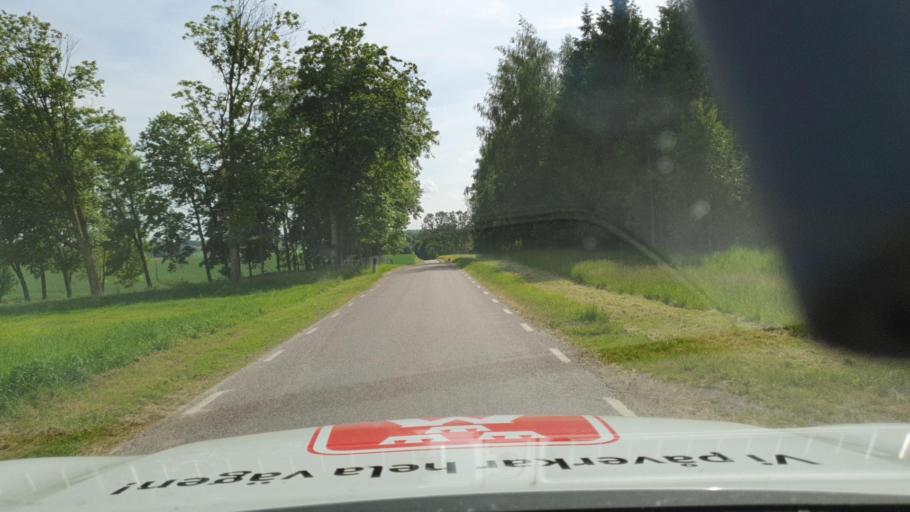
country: SE
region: Skane
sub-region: Skurups Kommun
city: Skurup
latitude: 55.5528
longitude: 13.4921
